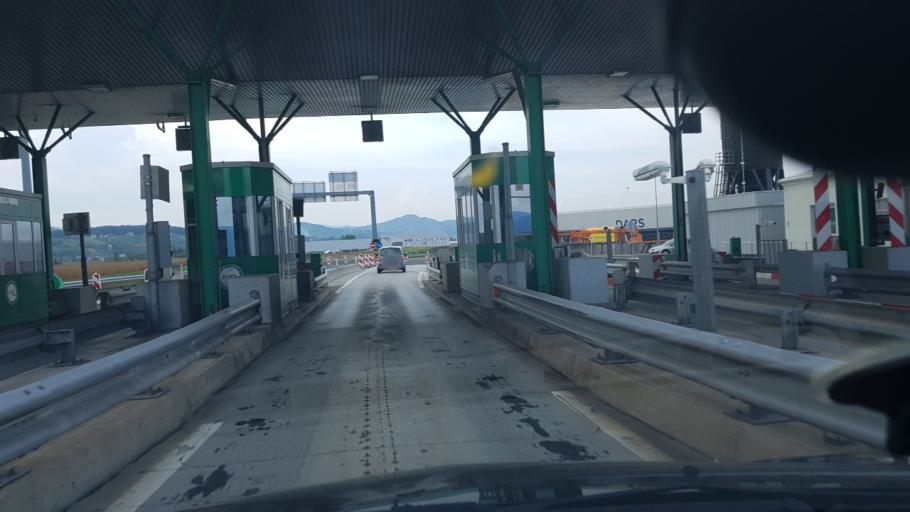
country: SI
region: Krsko
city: Leskovec pri Krskem
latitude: 45.9146
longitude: 15.4690
